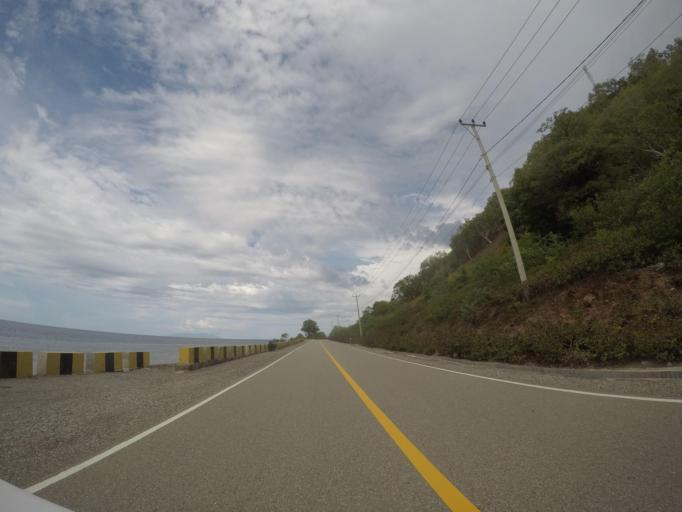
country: TL
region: Liquica
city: Maubara
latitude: -8.6122
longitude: 125.1940
